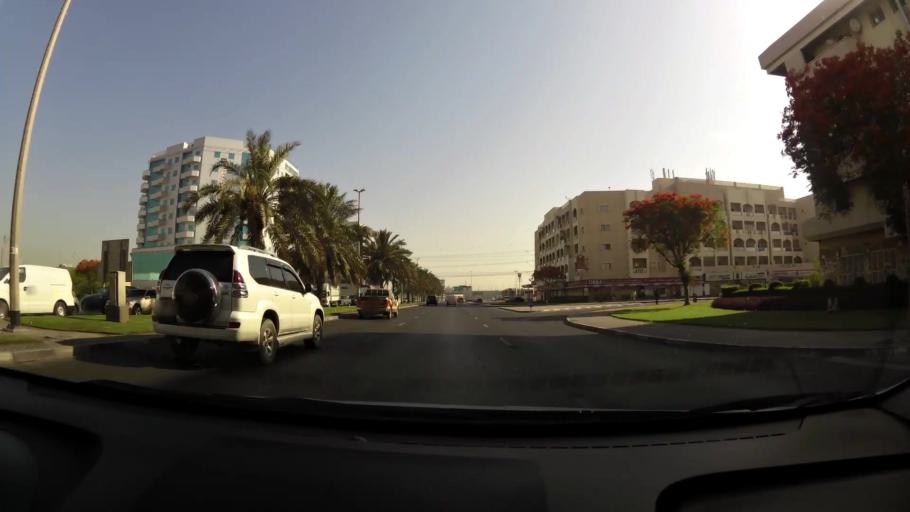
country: AE
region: Ash Shariqah
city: Sharjah
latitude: 25.2952
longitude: 55.3962
